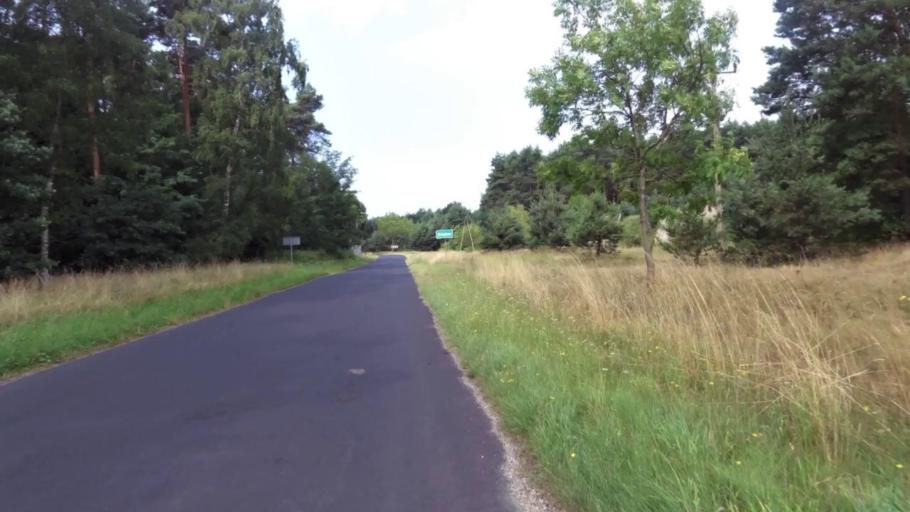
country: PL
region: West Pomeranian Voivodeship
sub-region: Powiat mysliborski
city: Debno
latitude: 52.8454
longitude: 14.7566
